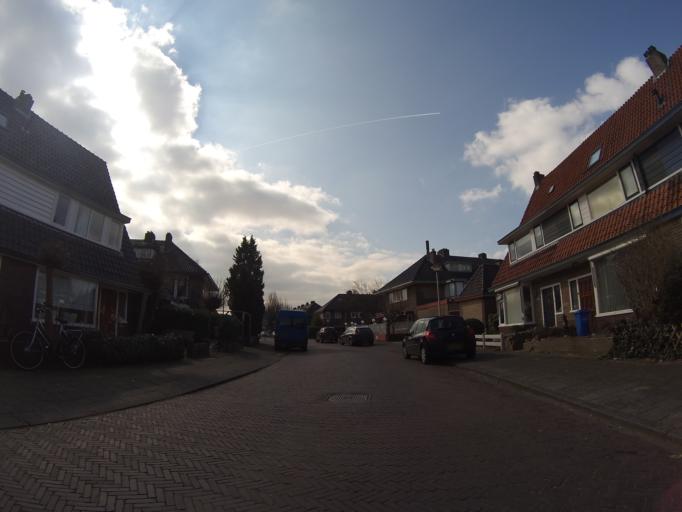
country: NL
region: Utrecht
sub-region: Gemeente Amersfoort
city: Amersfoort
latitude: 52.1444
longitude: 5.3844
